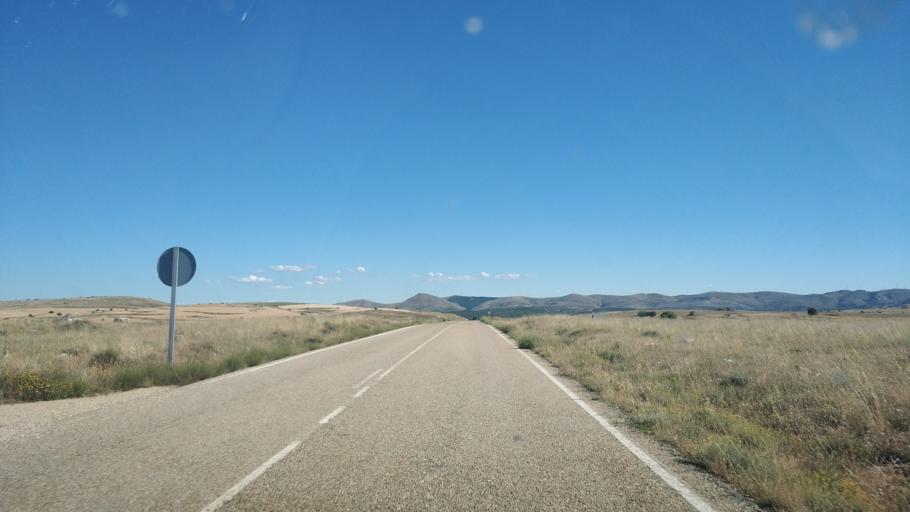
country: ES
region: Castille and Leon
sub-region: Provincia de Soria
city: Montejo de Tiermes
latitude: 41.3825
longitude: -3.1934
